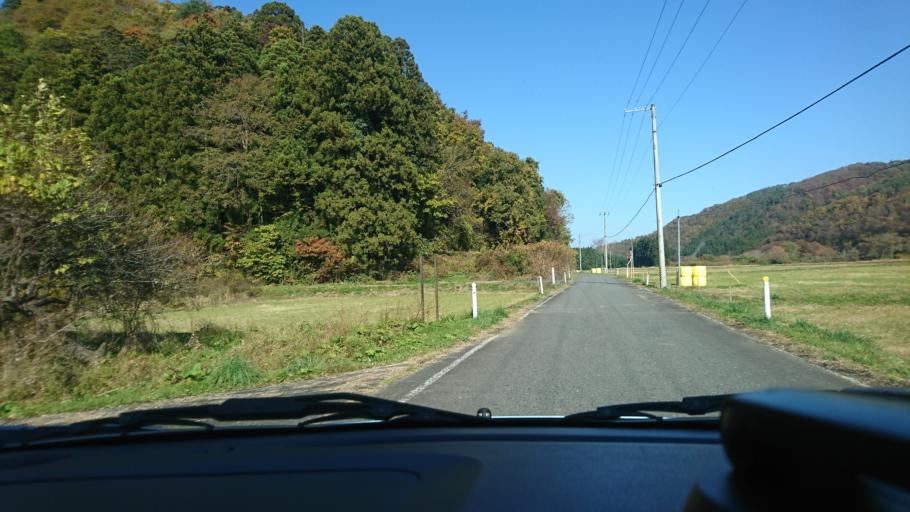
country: JP
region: Iwate
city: Ichinoseki
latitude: 38.8115
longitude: 141.2480
